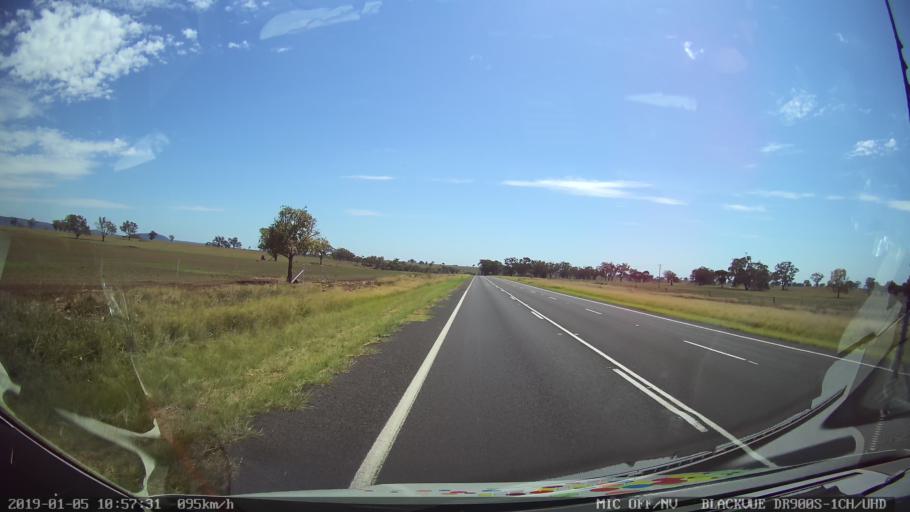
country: AU
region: New South Wales
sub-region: Warrumbungle Shire
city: Coonabarabran
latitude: -31.4306
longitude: 149.1707
